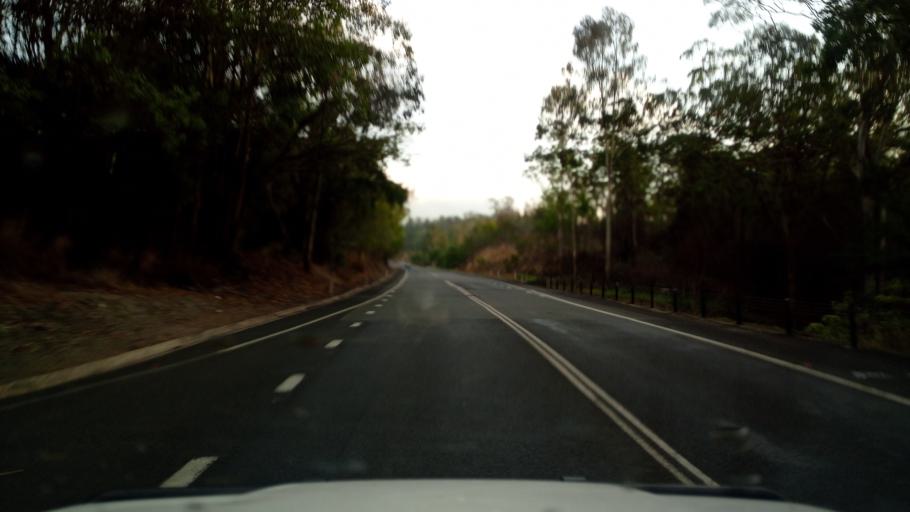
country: AU
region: Queensland
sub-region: Tablelands
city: Kuranda
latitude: -16.8507
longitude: 145.6013
